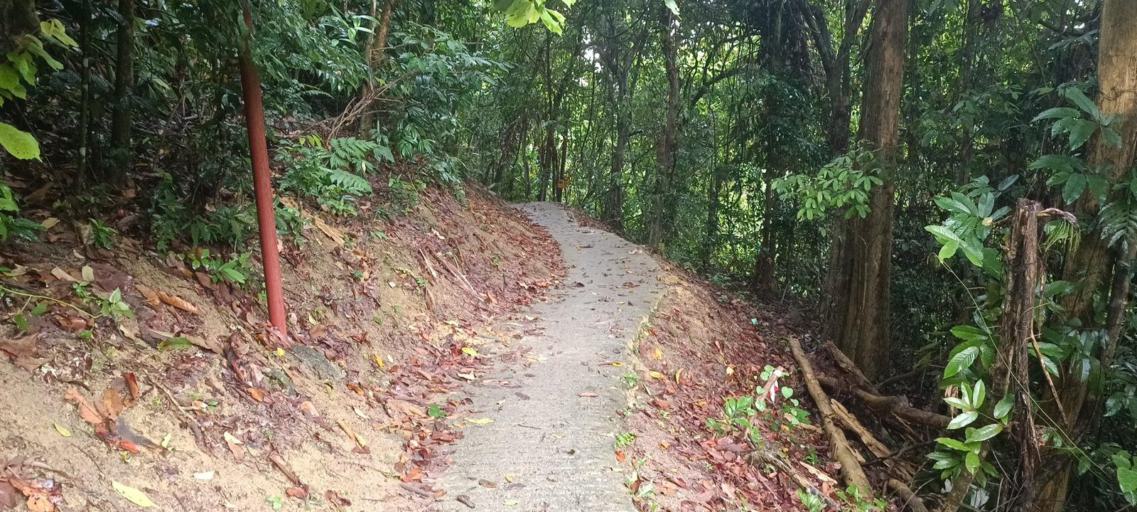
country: MY
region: Penang
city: Bukit Mertajam
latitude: 5.3645
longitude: 100.4702
